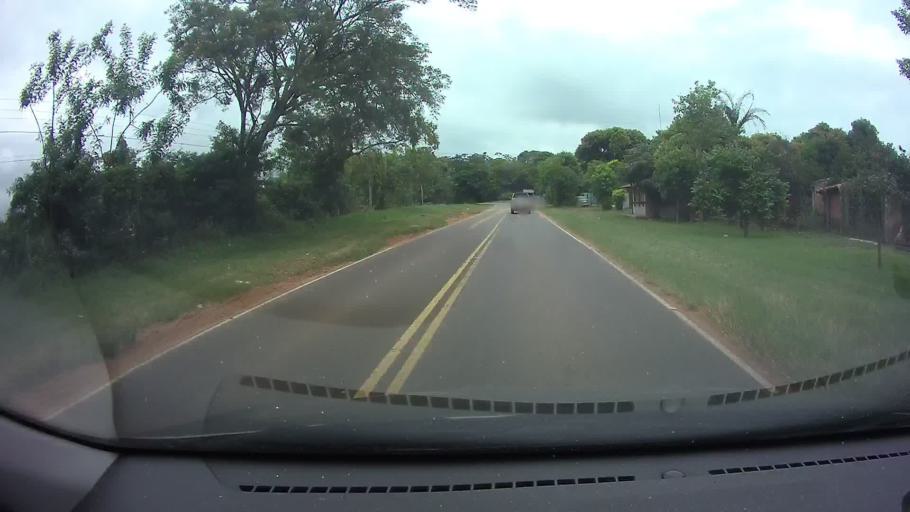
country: PY
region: Central
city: Nueva Italia
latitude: -25.5933
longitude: -57.5080
